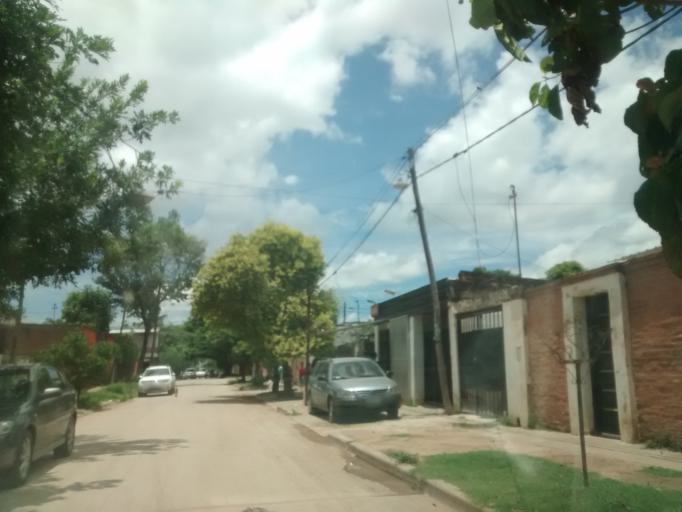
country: AR
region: Chaco
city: Fontana
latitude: -27.4313
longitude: -59.0008
